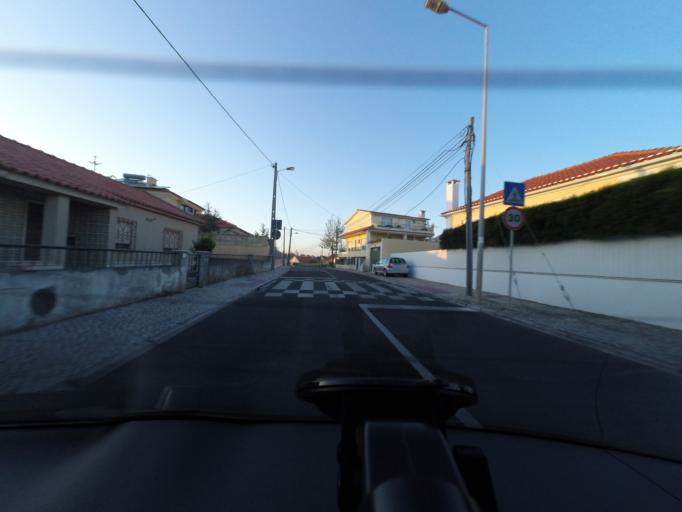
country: PT
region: Lisbon
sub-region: Cascais
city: Sao Domingos de Rana
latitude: 38.7271
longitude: -9.3431
